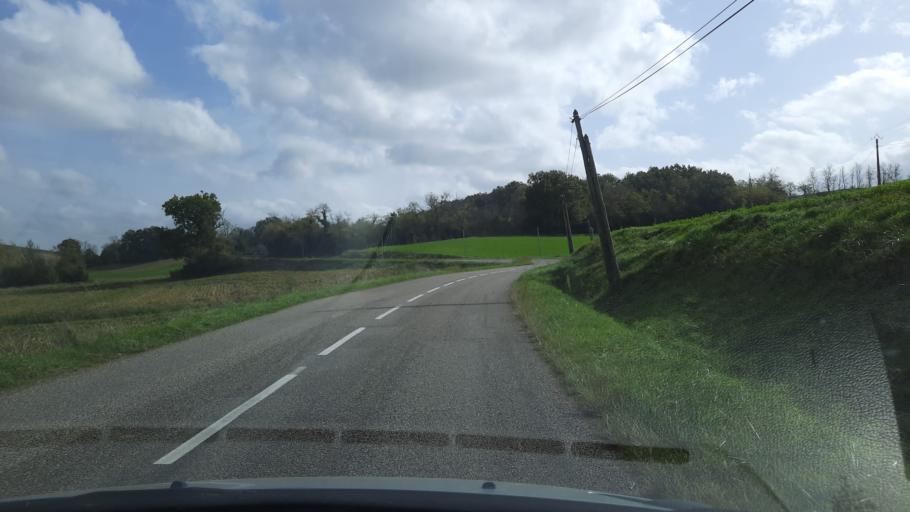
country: FR
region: Midi-Pyrenees
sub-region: Departement du Tarn-et-Garonne
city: Molieres
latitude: 44.1871
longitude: 1.2897
